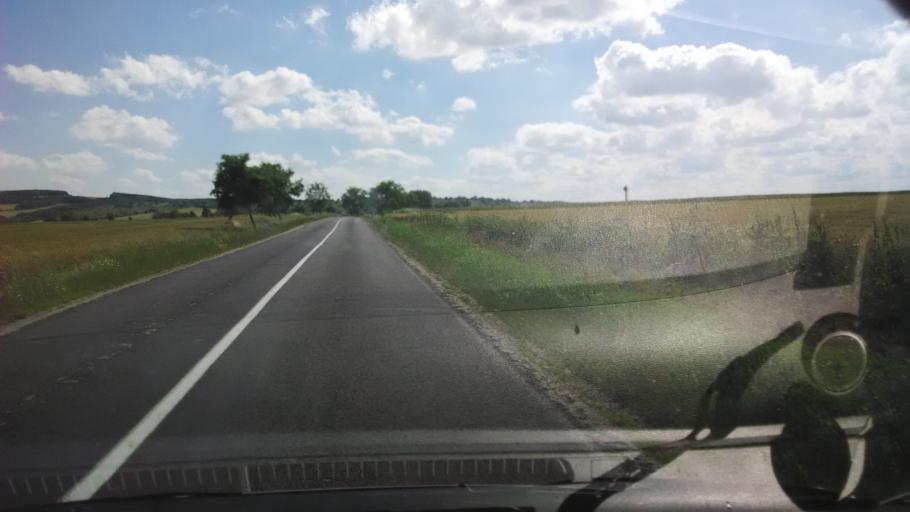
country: SK
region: Nitriansky
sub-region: Okres Nitra
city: Vrable
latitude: 48.1239
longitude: 18.3898
